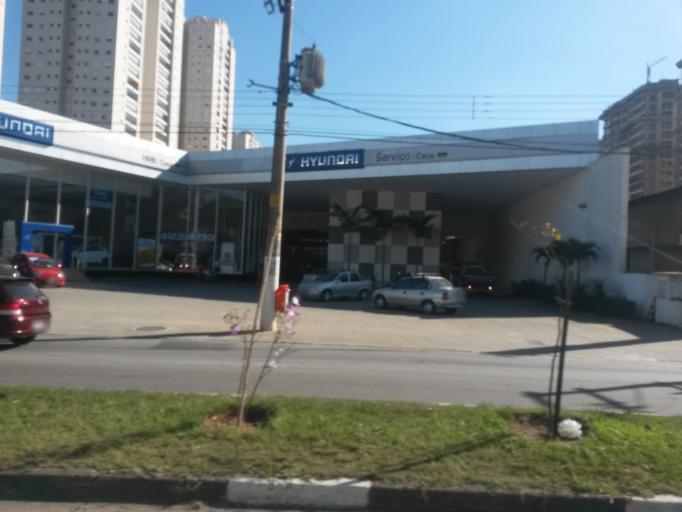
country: BR
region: Sao Paulo
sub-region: Sao Bernardo Do Campo
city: Sao Bernardo do Campo
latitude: -23.6863
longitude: -46.5476
